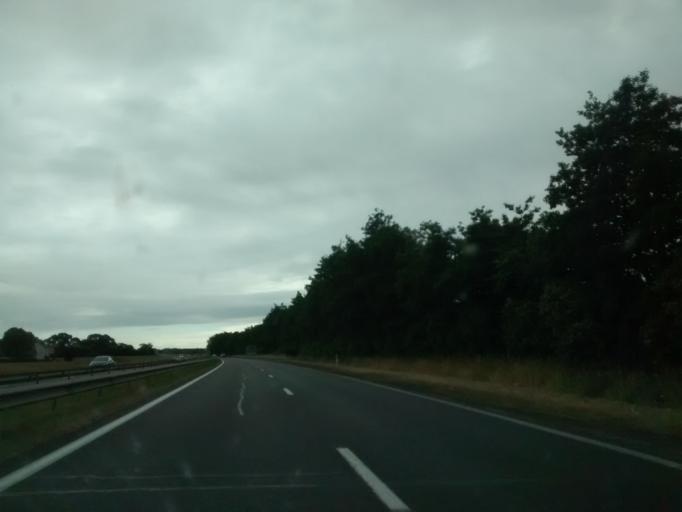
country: FR
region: Brittany
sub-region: Departement des Cotes-d'Armor
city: Tremuson
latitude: 48.5420
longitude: -2.8371
